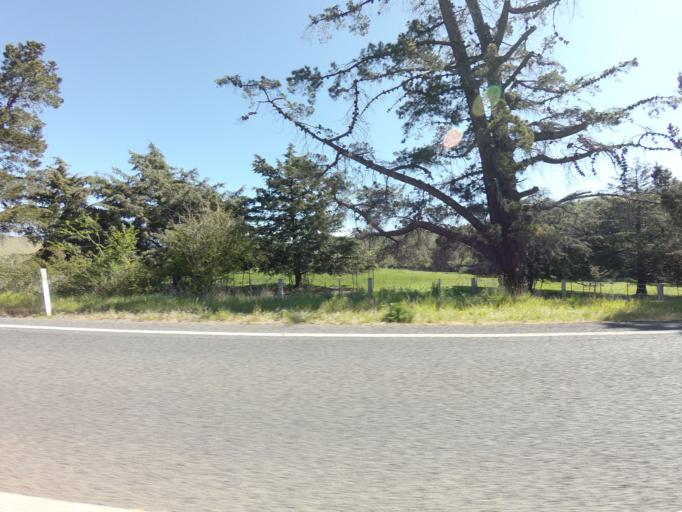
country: AU
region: Tasmania
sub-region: Derwent Valley
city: New Norfolk
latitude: -42.5650
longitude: 146.8800
